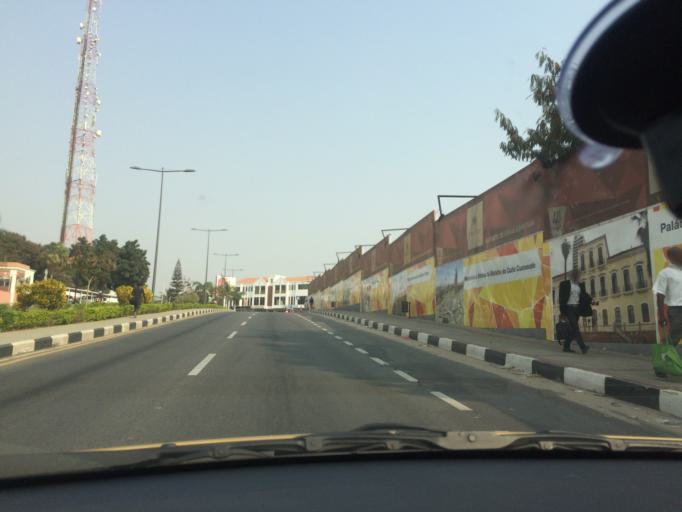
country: AO
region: Luanda
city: Luanda
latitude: -8.8234
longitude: 13.2234
